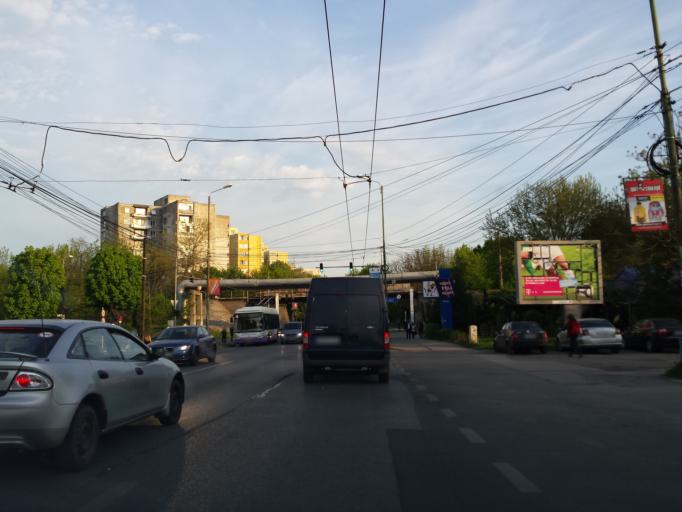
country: RO
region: Timis
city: Timisoara
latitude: 45.7628
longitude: 21.2260
